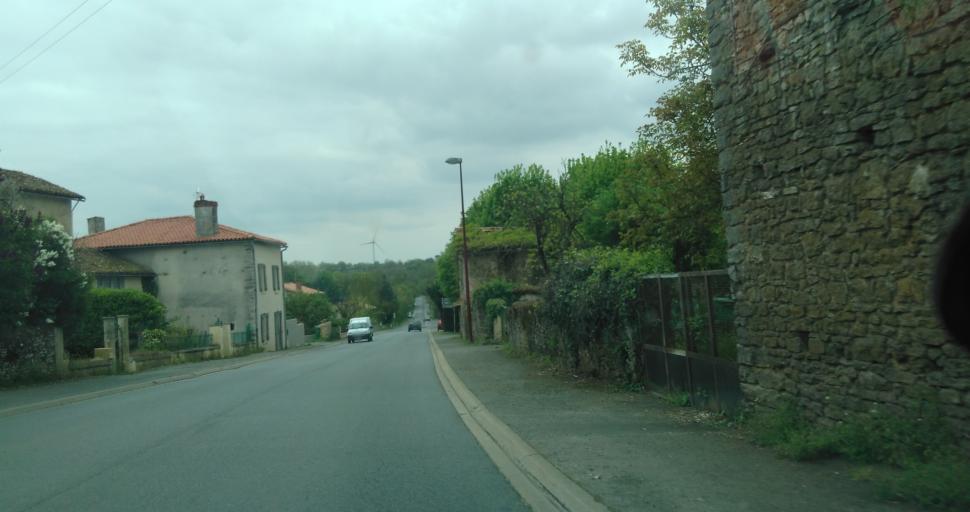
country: FR
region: Poitou-Charentes
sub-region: Departement des Deux-Sevres
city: Champdeniers-Saint-Denis
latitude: 46.4847
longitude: -0.3989
